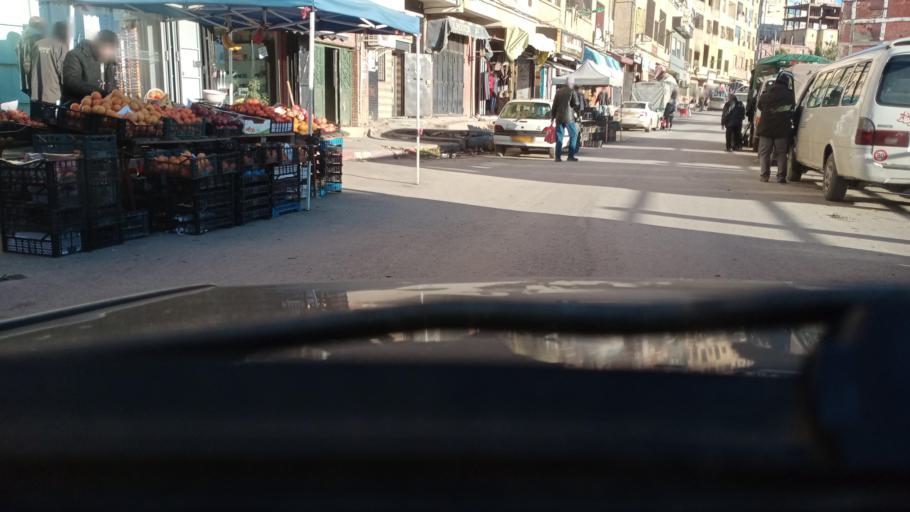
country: DZ
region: Tizi Ouzou
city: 'Ain el Hammam
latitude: 36.5735
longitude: 4.3071
